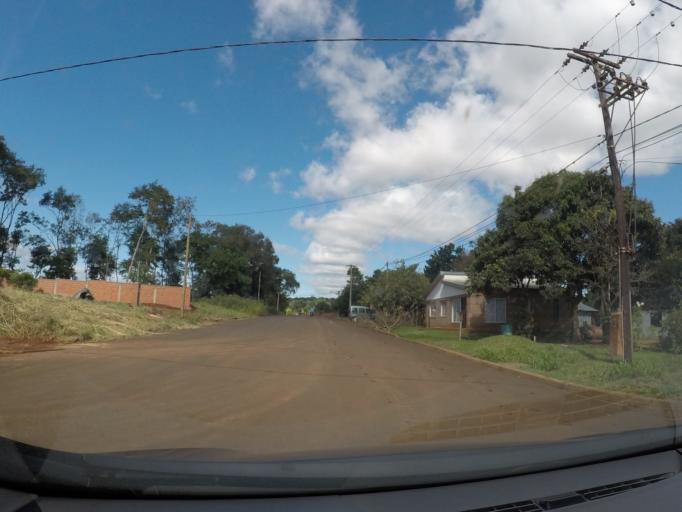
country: AR
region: Misiones
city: Puerto Rico
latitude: -26.7986
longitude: -55.0136
